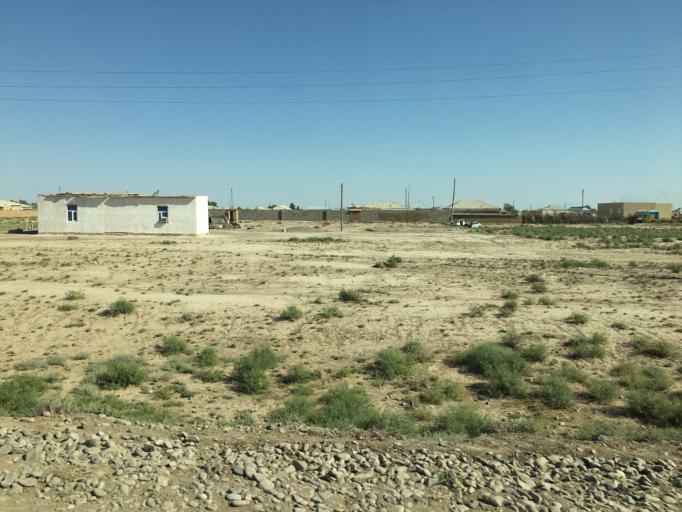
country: IR
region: Razavi Khorasan
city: Sarakhs
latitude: 36.5757
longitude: 61.2649
